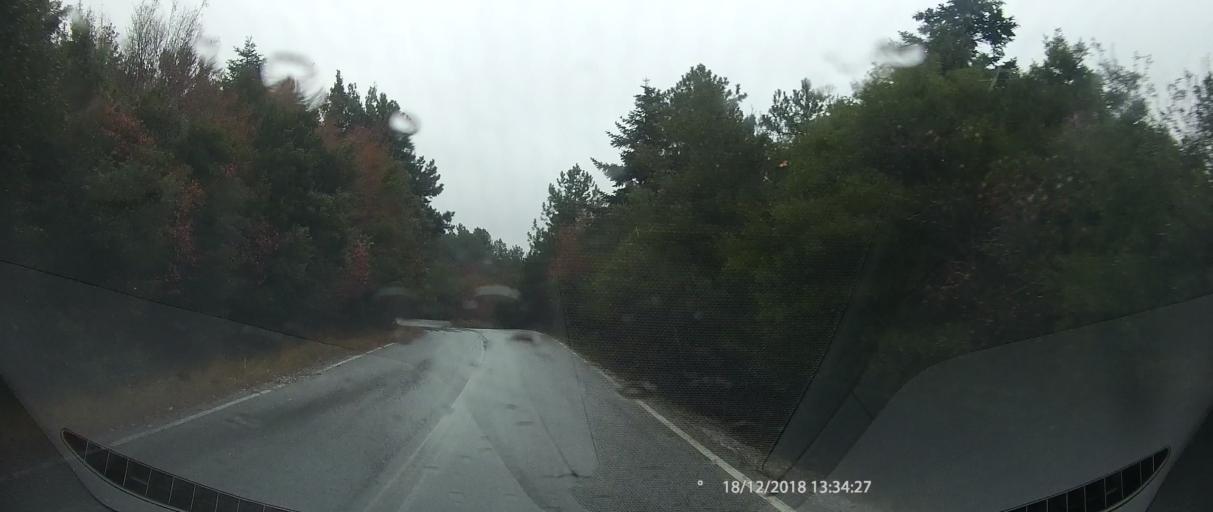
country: GR
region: Central Macedonia
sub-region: Nomos Pierias
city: Litochoro
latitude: 40.1128
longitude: 22.4859
